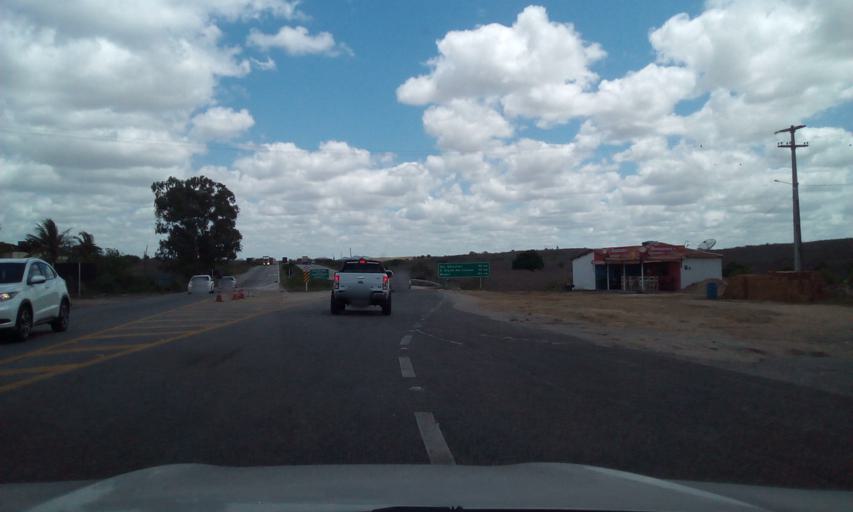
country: BR
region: Alagoas
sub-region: Porto Real Do Colegio
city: Porto Real do Colegio
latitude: -10.1791
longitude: -36.8270
